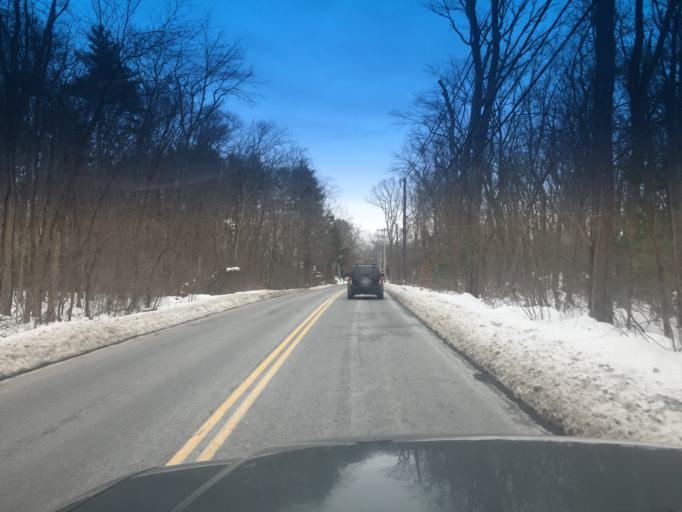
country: US
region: Massachusetts
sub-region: Norfolk County
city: Norfolk
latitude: 42.1135
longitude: -71.2869
